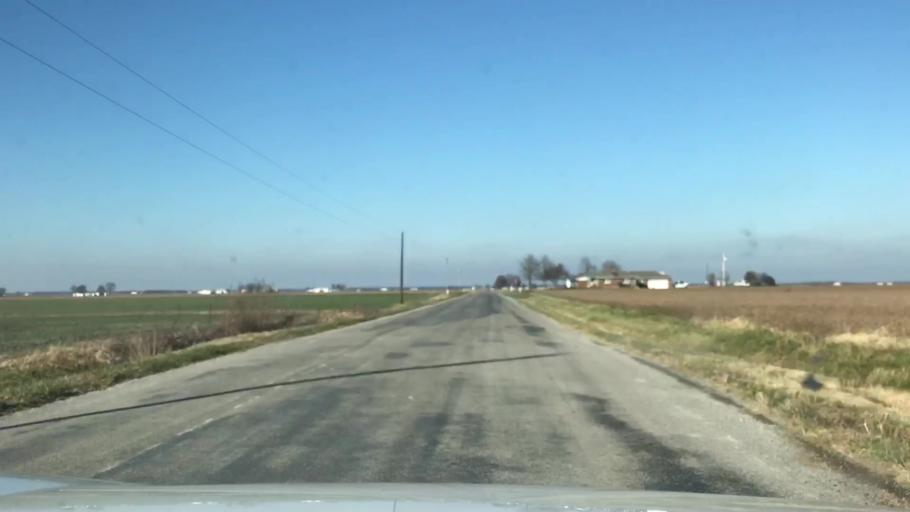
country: US
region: Illinois
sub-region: Washington County
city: Okawville
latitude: 38.4036
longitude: -89.4865
